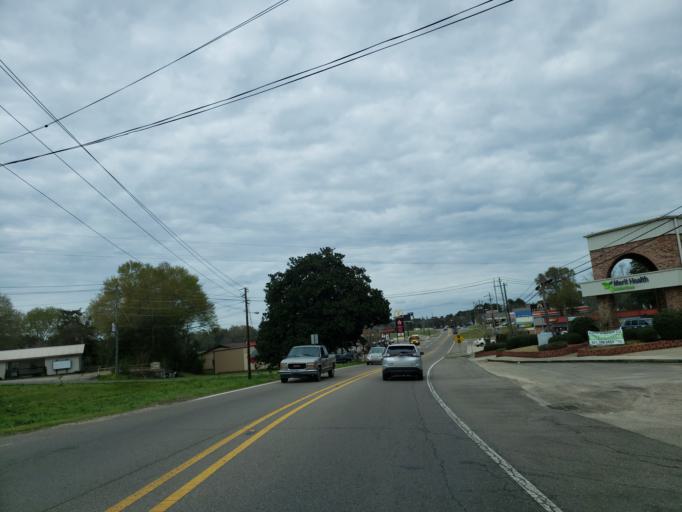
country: US
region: Mississippi
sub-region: Lamar County
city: Purvis
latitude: 31.1436
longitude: -89.4051
